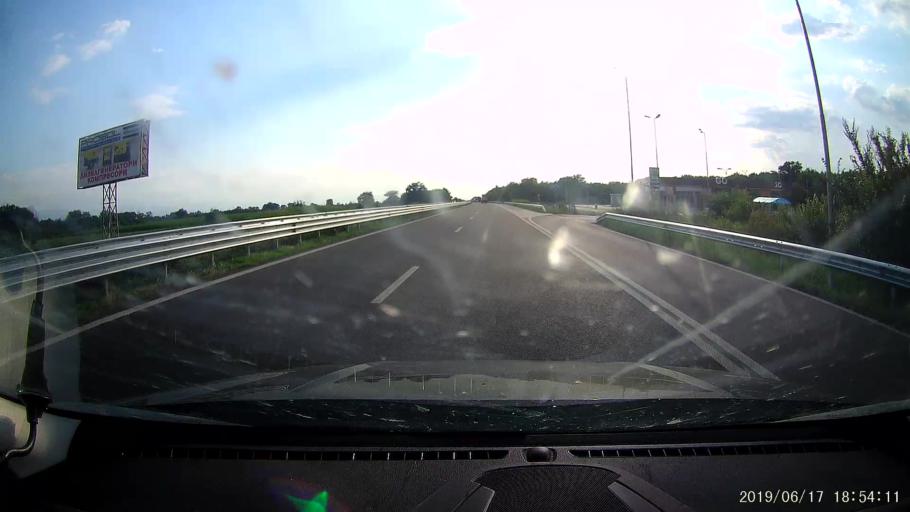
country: BG
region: Plovdiv
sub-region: Obshtina Sadovo
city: Sadovo
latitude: 42.2182
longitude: 24.8896
